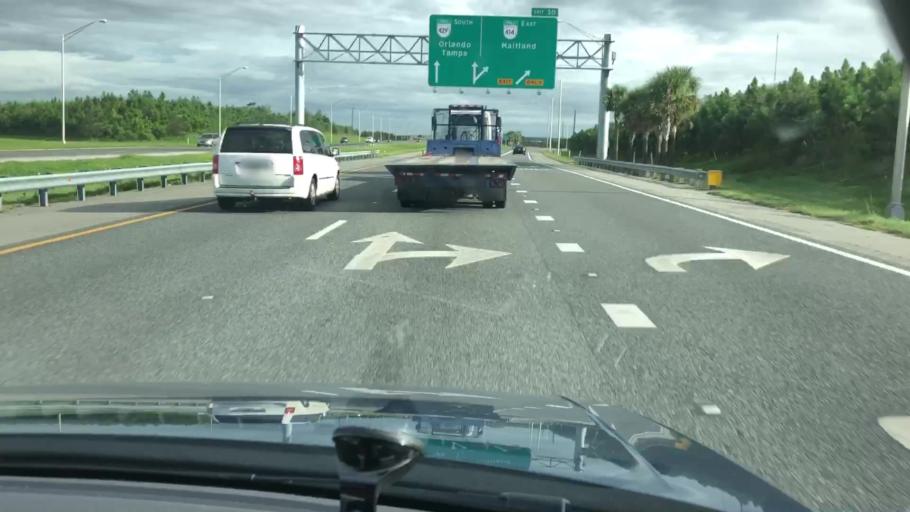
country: US
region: Florida
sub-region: Orange County
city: Paradise Heights
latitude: 28.6580
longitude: -81.5502
